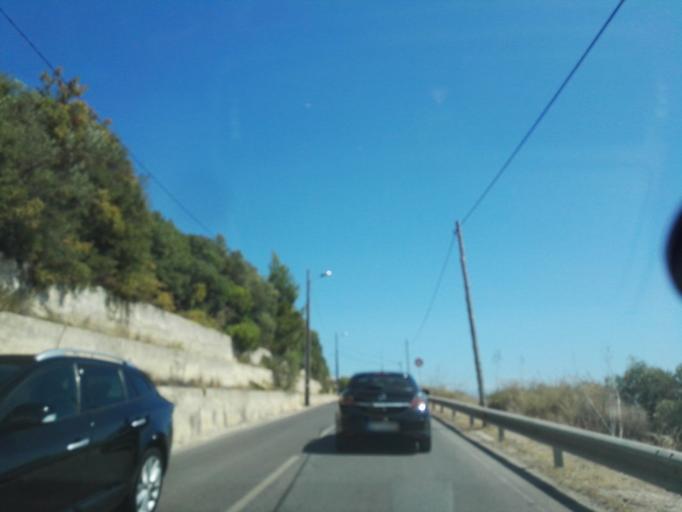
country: PT
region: Setubal
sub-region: Sesimbra
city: Sesimbra
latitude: 38.4422
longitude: -9.0905
